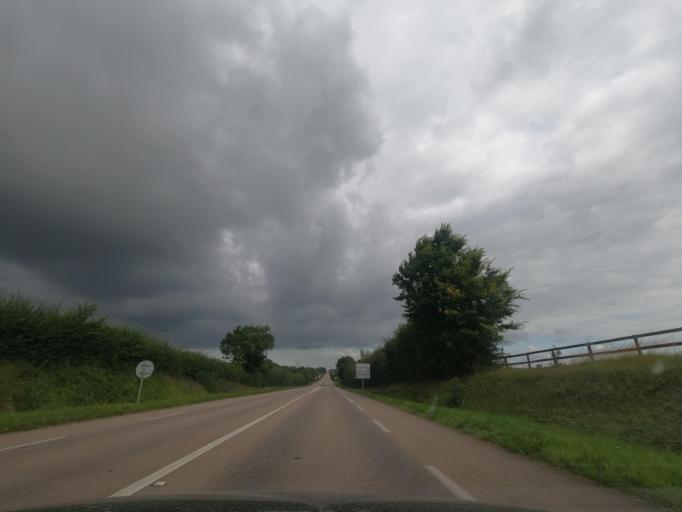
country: FR
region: Lower Normandy
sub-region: Departement de l'Orne
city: Argentan
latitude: 48.7491
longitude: 0.0184
